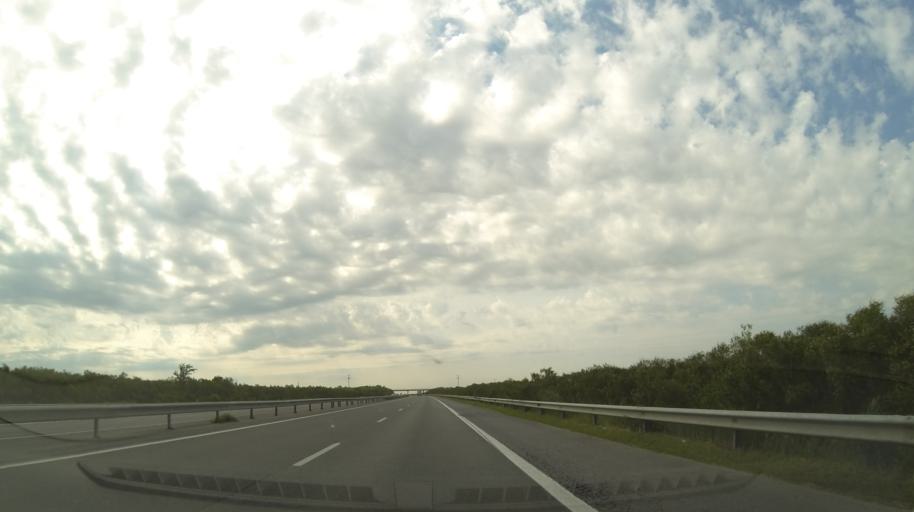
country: RO
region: Arges
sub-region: Comuna Ratesti
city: Ratesti
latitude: 44.7398
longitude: 25.1077
